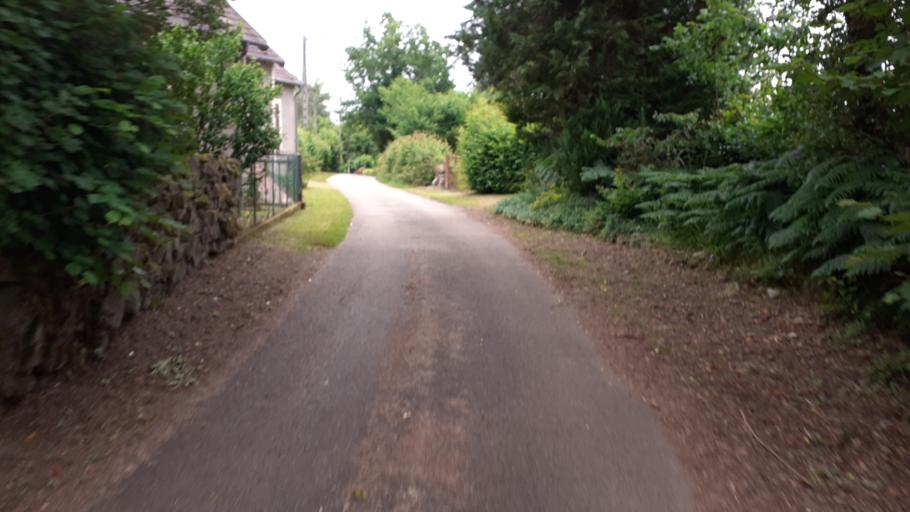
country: FR
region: Bourgogne
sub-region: Departement de la Cote-d'Or
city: Saulieu
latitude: 47.2705
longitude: 4.1404
